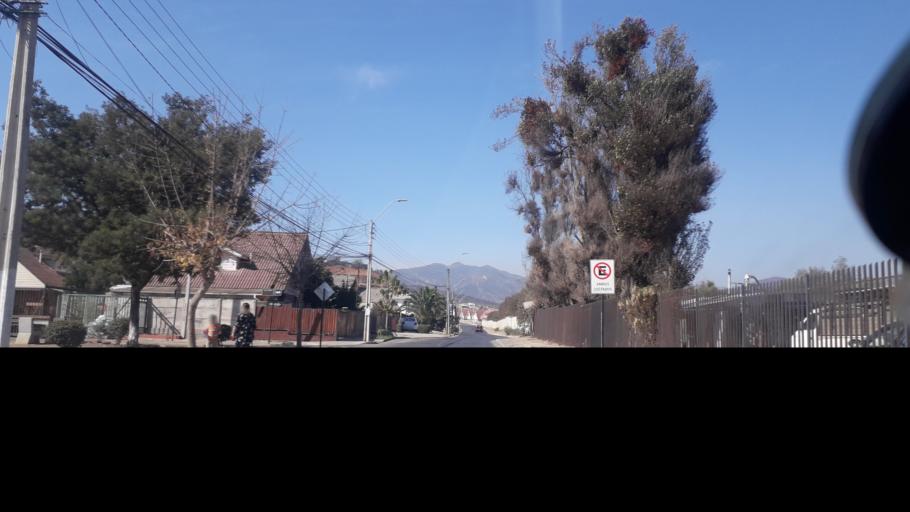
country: CL
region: Valparaiso
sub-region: Provincia de Marga Marga
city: Villa Alemana
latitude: -33.0478
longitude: -71.3467
